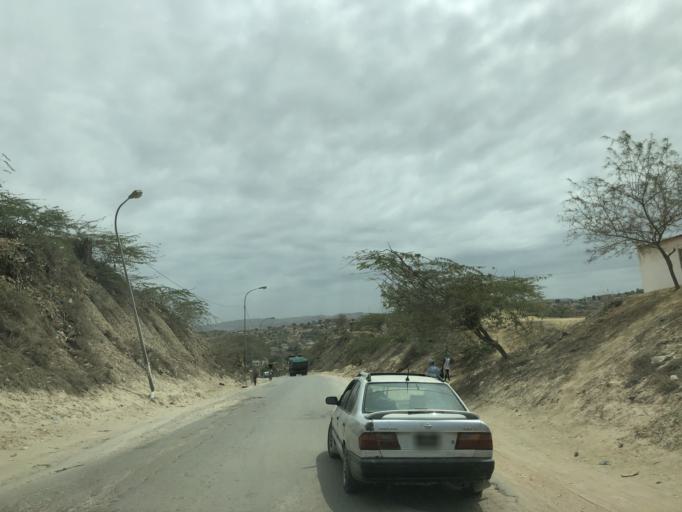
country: AO
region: Cuanza Sul
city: Sumbe
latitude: -11.2235
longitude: 13.8464
